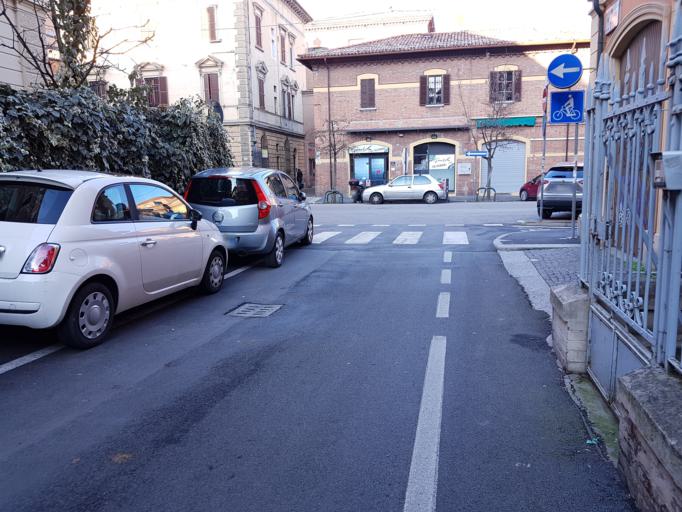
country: IT
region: Emilia-Romagna
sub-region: Provincia di Bologna
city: Bologna
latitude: 44.4855
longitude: 11.3592
